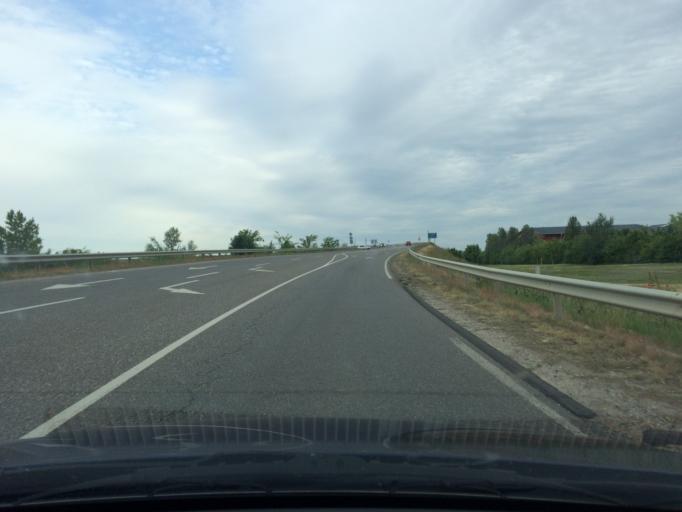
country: HU
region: Hajdu-Bihar
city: Hajdunanas
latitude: 47.8854
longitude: 21.4143
